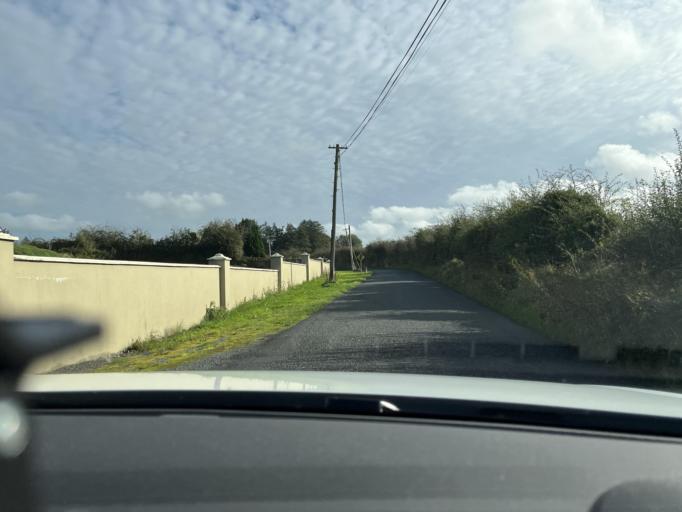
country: IE
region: Connaught
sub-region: Sligo
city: Ballymote
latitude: 54.0786
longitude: -8.4132
